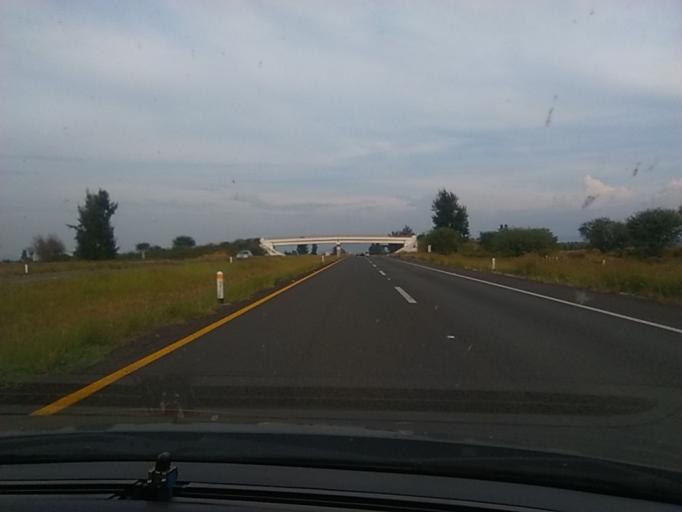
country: MX
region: Michoacan
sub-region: Alvaro Obregon
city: Tzintzimeo
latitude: 19.8914
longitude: -100.9993
